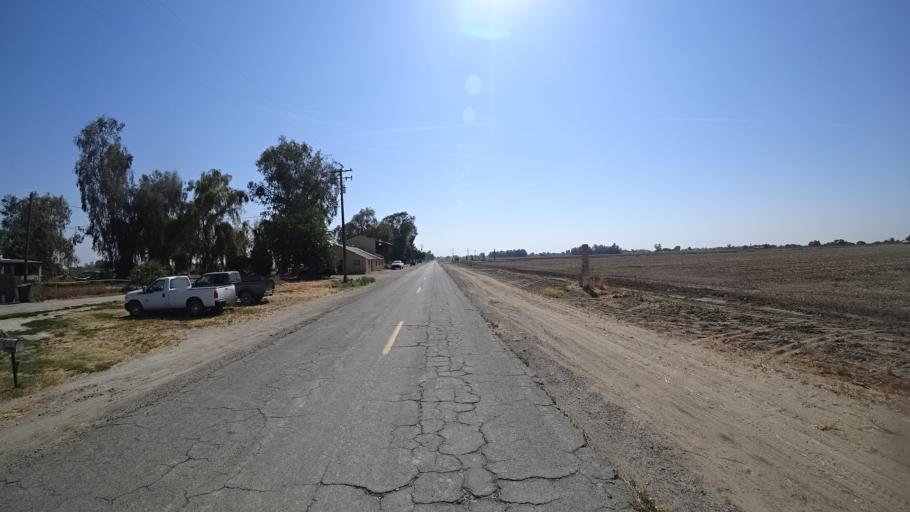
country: US
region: California
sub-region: Fresno County
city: Riverdale
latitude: 36.3512
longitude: -119.8808
